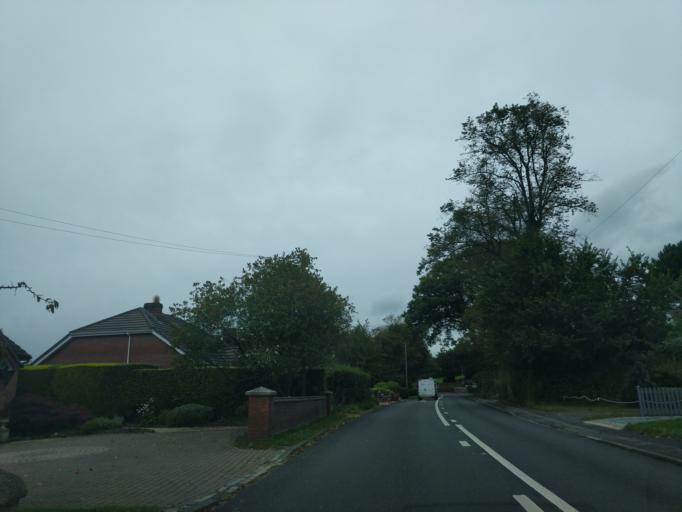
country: GB
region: England
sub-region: Cheshire East
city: Chorlton
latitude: 53.0273
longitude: -2.3680
